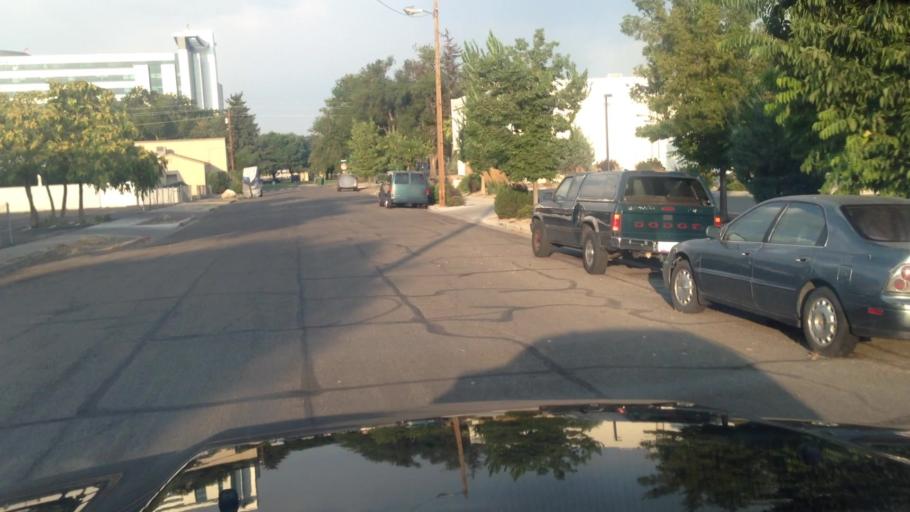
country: US
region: Nevada
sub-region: Washoe County
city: Reno
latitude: 39.5247
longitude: -119.8001
